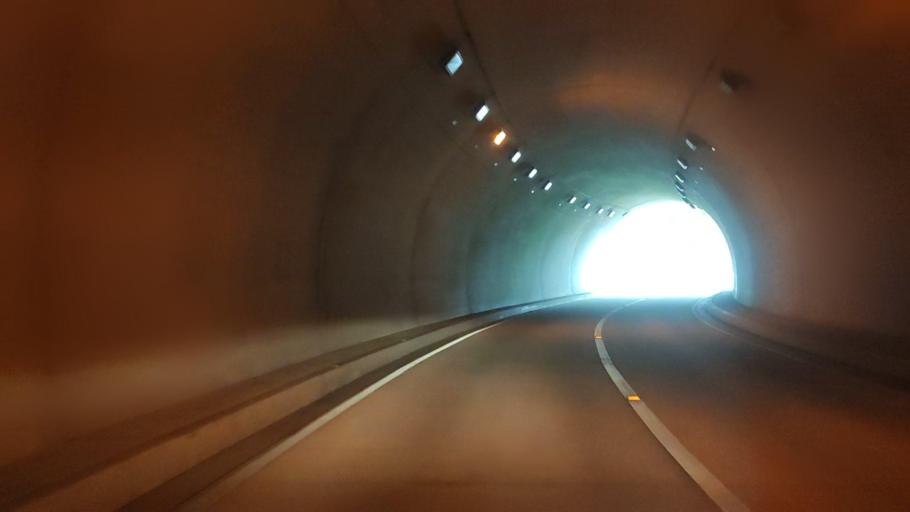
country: JP
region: Nagasaki
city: Shimabara
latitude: 32.7614
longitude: 130.2778
